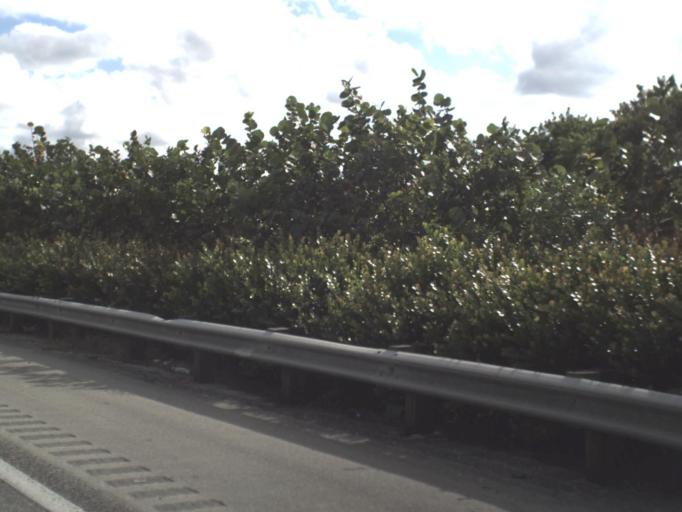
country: US
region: Florida
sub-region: Saint Lucie County
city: Port Saint Lucie
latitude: 27.2635
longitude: -80.3530
